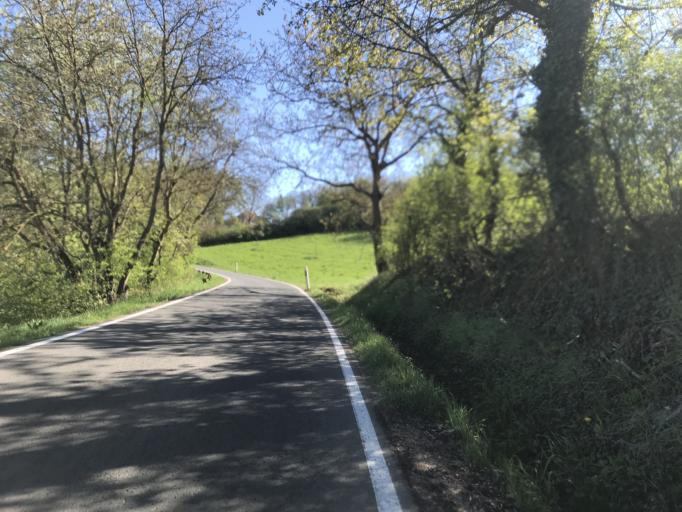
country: DE
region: Rheinland-Pfalz
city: Appenheim
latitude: 49.9445
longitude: 8.0553
